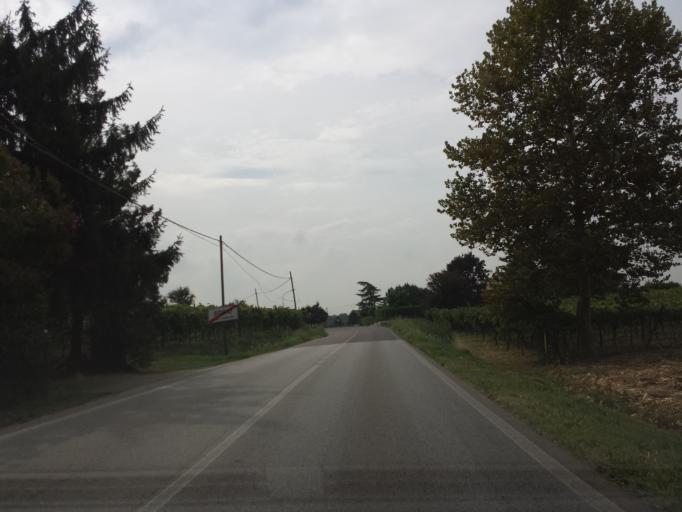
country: IT
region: Veneto
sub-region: Provincia di Vicenza
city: Gambellara
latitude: 45.4459
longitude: 11.3532
